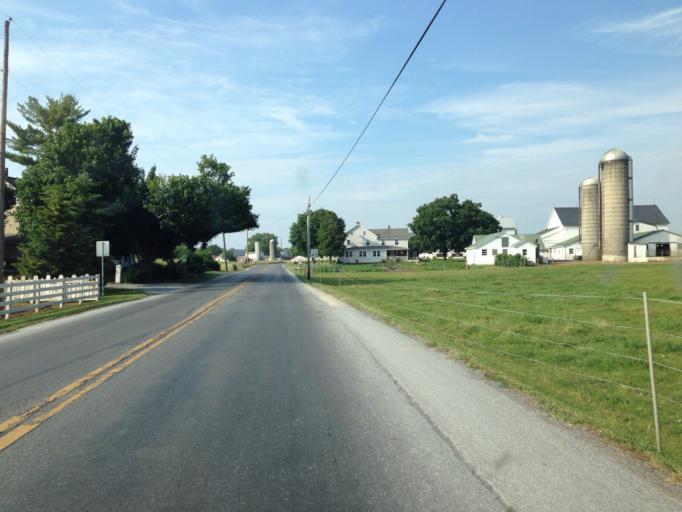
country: US
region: Pennsylvania
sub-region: Lancaster County
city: Brownstown
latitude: 40.0590
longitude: -76.2129
